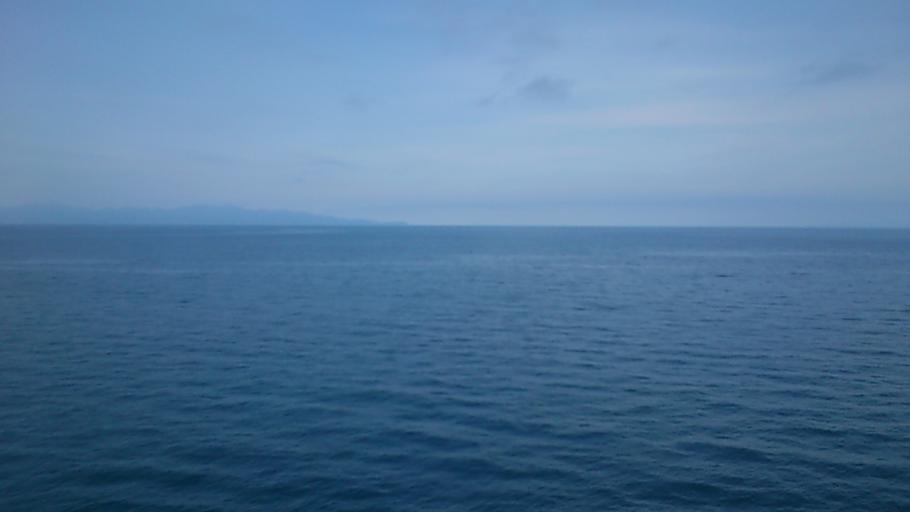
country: JP
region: Aomori
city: Aomori Shi
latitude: 41.2909
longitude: 140.6607
